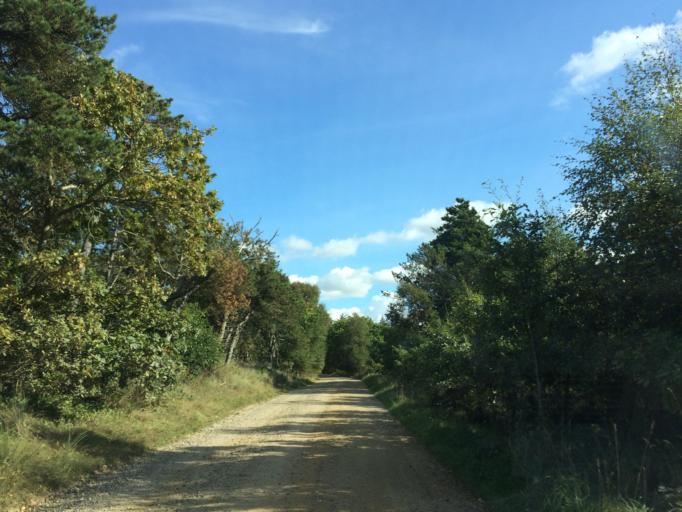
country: DK
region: Central Jutland
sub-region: Holstebro Kommune
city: Ulfborg
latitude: 56.2842
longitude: 8.1556
